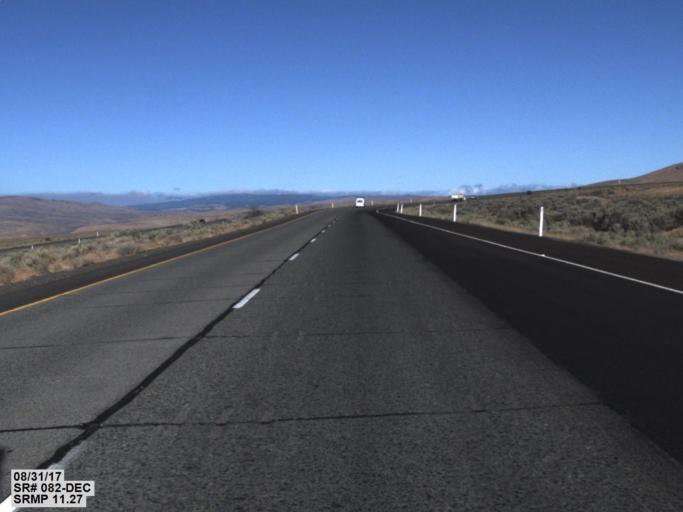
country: US
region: Washington
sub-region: Kittitas County
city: Kittitas
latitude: 46.8469
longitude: -120.3837
